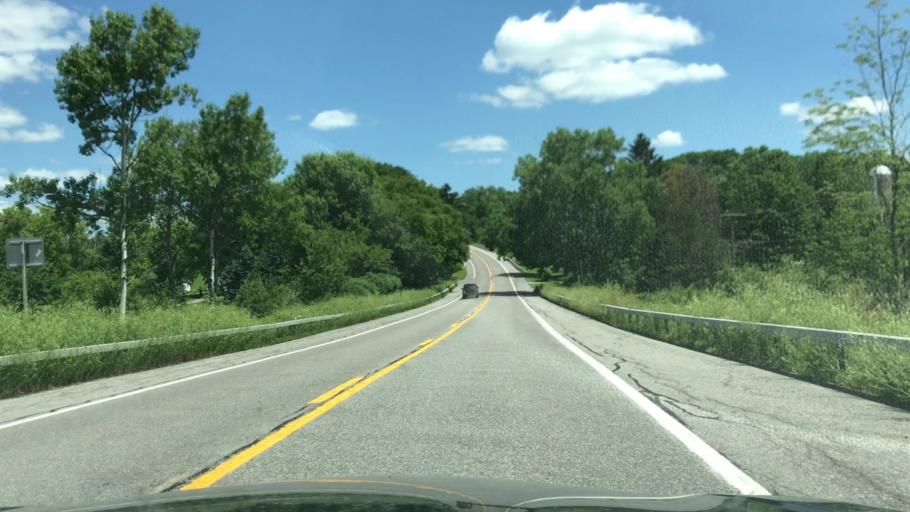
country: US
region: New York
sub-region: Erie County
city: East Aurora
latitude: 42.7697
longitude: -78.4877
